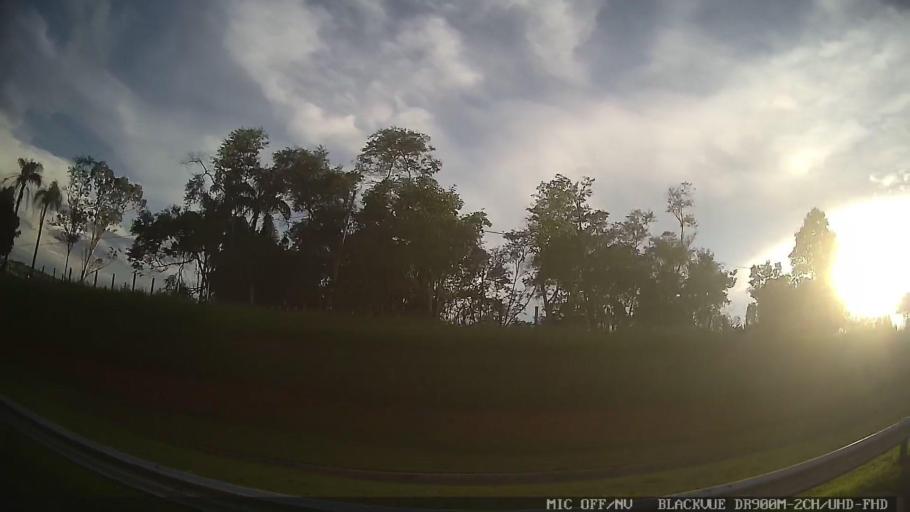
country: BR
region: Sao Paulo
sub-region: Tiete
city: Tiete
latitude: -23.1588
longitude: -47.6505
